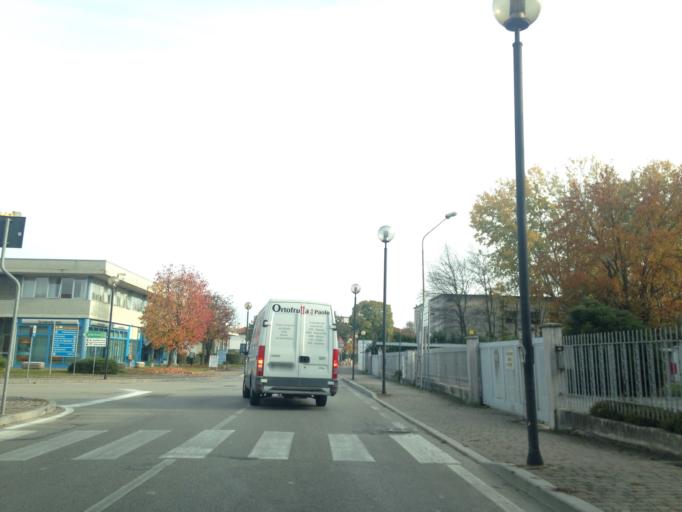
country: IT
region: Friuli Venezia Giulia
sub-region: Provincia di Pordenone
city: Brugnera
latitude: 45.9002
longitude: 12.5341
